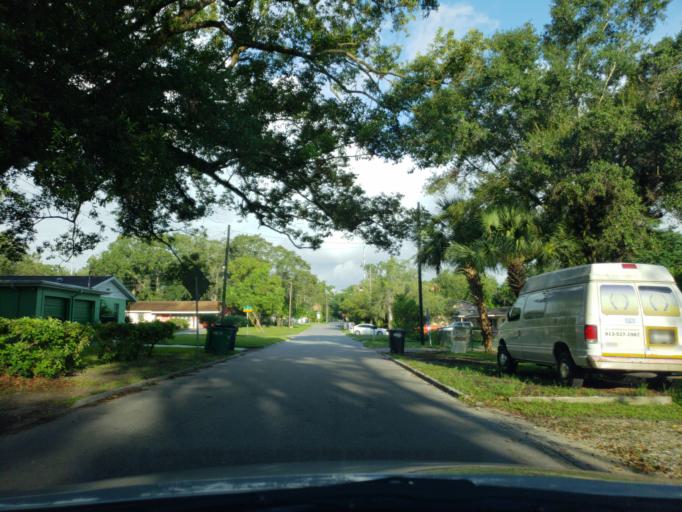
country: US
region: Florida
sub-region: Hillsborough County
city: East Lake-Orient Park
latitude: 27.9906
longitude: -82.4169
